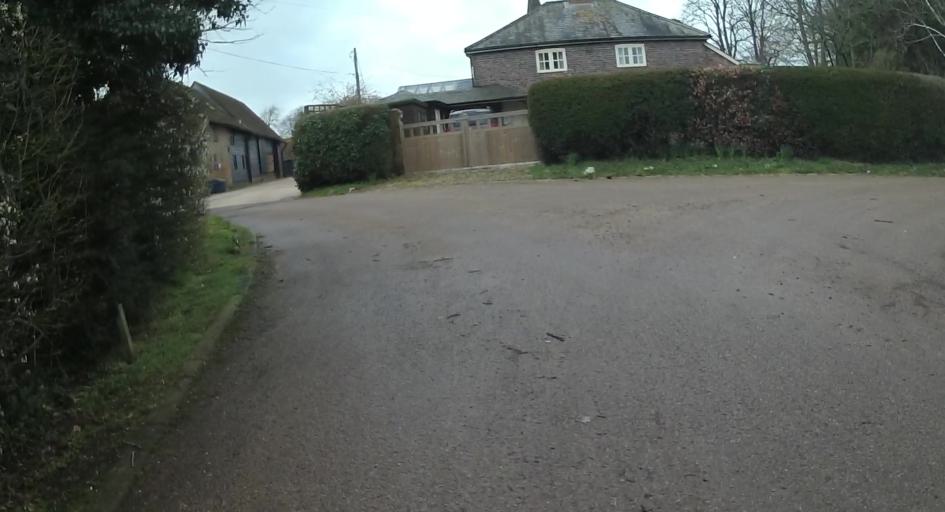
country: GB
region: England
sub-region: Hampshire
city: Kingsclere
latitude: 51.2955
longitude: -1.2280
